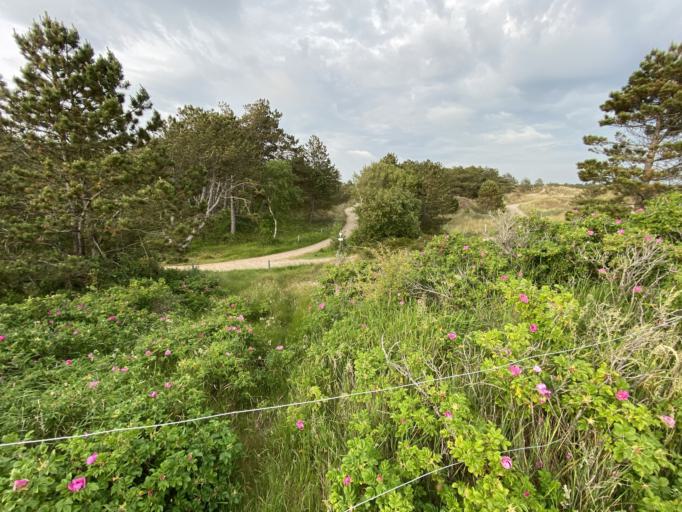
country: DE
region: Schleswig-Holstein
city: Sankt Peter-Ording
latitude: 54.3185
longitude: 8.6027
